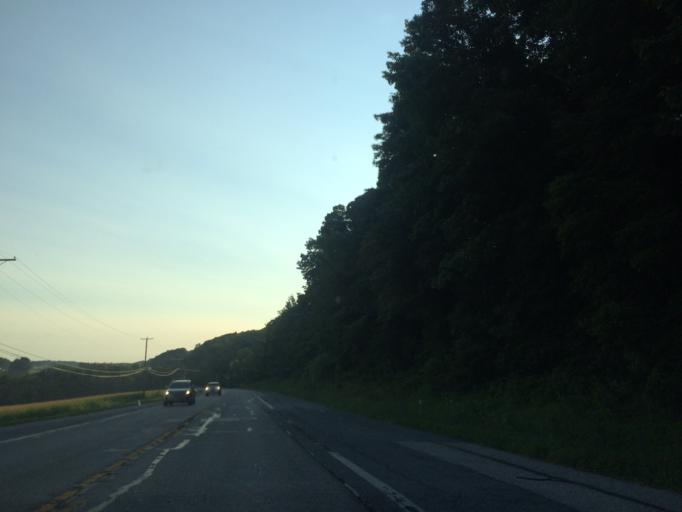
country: US
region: Maryland
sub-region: Carroll County
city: Manchester
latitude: 39.6332
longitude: -76.9294
